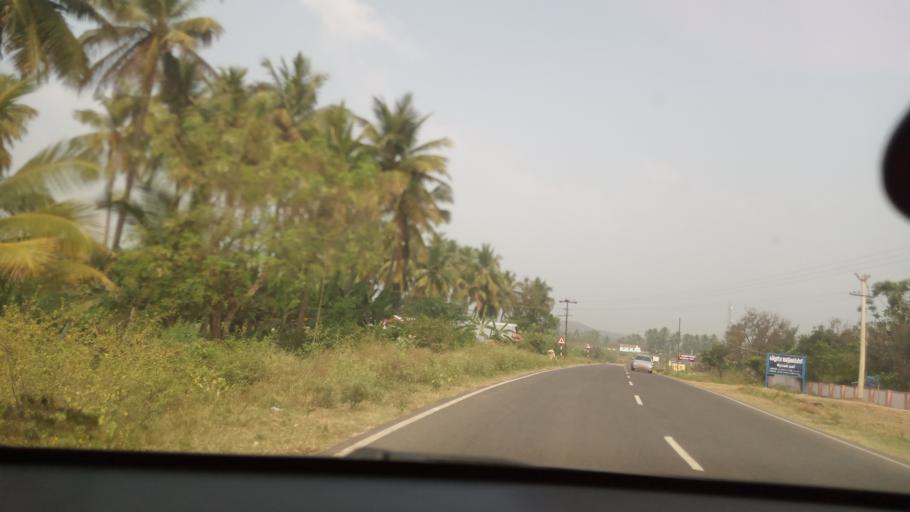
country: IN
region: Tamil Nadu
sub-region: Erode
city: Sathyamangalam
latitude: 11.5303
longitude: 77.1398
